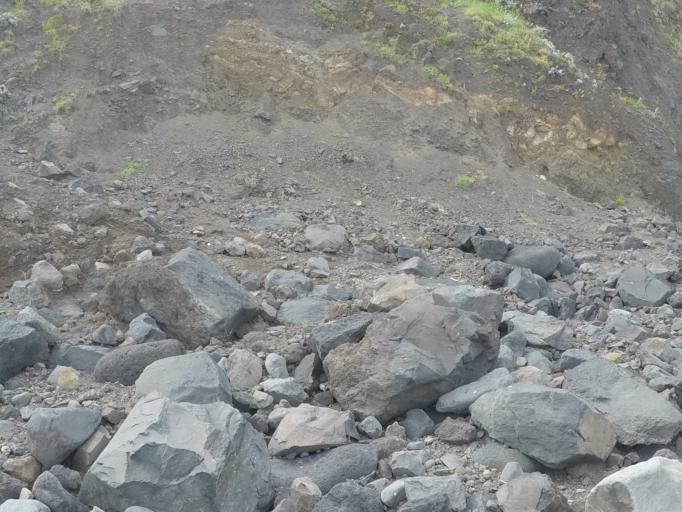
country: PT
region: Madeira
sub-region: Sao Vicente
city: Sao Vicente
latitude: 32.8270
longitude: -16.9972
